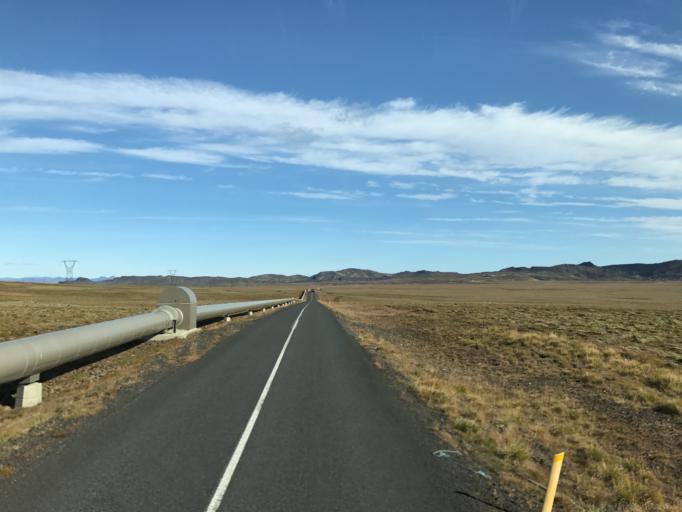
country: IS
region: South
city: Hveragerdi
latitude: 64.1204
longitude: -21.4170
